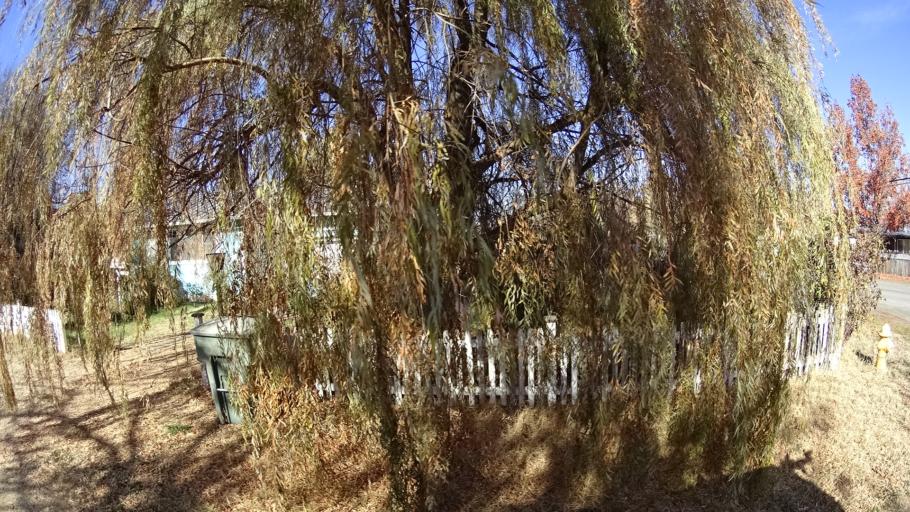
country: US
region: California
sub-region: Siskiyou County
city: Montague
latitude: 41.6433
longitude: -122.5225
